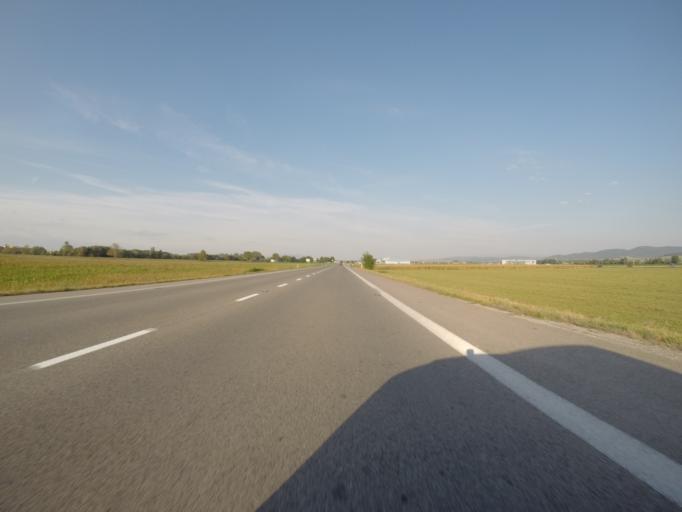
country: SK
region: Nitriansky
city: Banovce nad Bebravou
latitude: 48.5556
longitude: 18.1900
